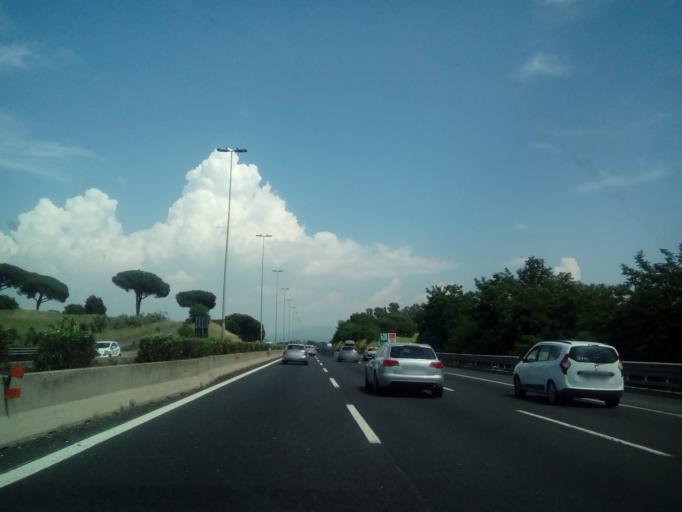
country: IT
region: Latium
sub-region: Citta metropolitana di Roma Capitale
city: Selcetta
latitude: 41.7960
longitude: 12.4938
